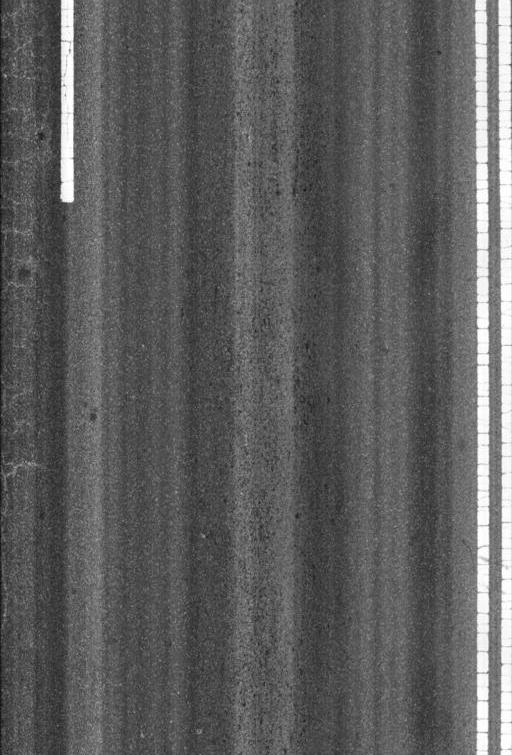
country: US
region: Maryland
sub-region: Prince George's County
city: Hillcrest Heights
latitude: 38.8369
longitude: -76.9812
